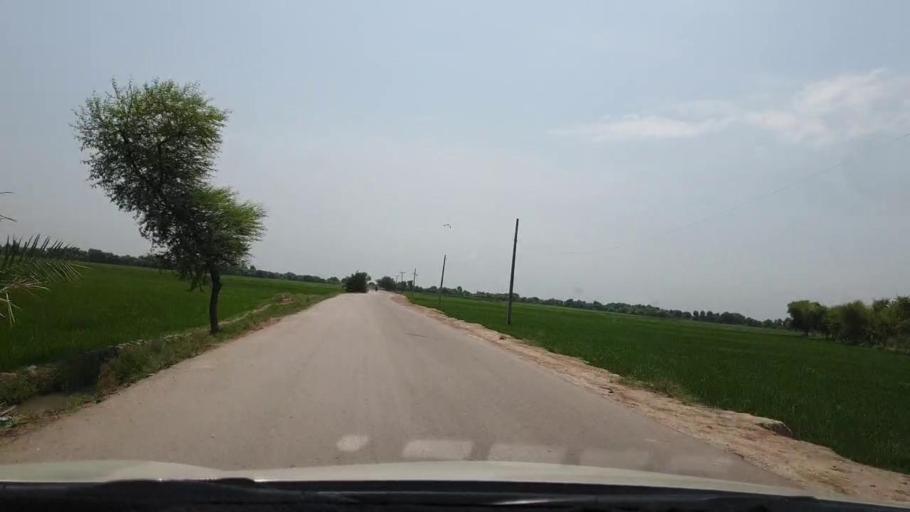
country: PK
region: Sindh
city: Ratodero
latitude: 27.8218
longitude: 68.2438
